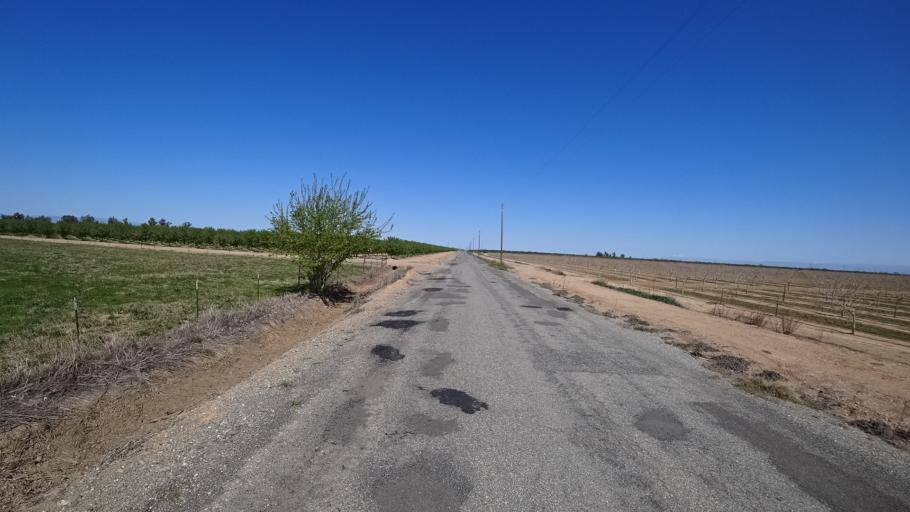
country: US
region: California
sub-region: Glenn County
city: Willows
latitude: 39.6351
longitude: -122.2347
